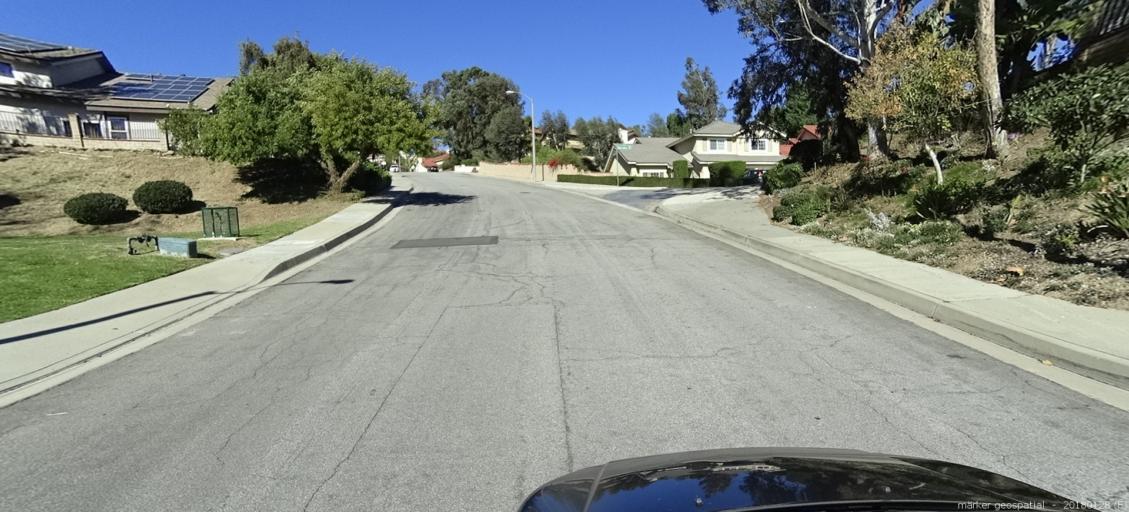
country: US
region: California
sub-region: San Bernardino County
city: Chino Hills
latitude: 33.9976
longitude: -117.7938
